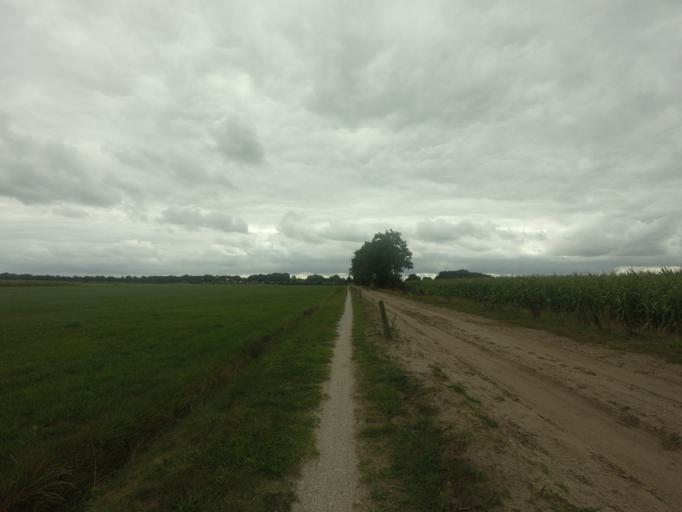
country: NL
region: Friesland
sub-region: Gemeente Weststellingwerf
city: Noordwolde
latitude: 52.9154
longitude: 6.1974
